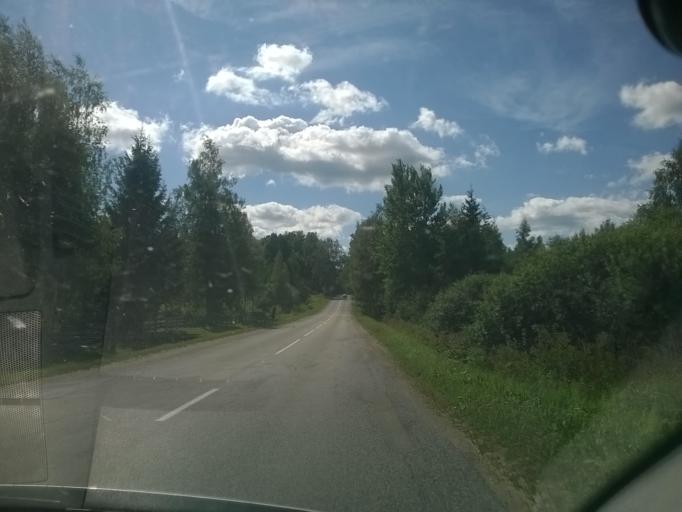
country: LV
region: Aluksnes Rajons
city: Aluksne
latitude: 57.4440
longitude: 27.0358
